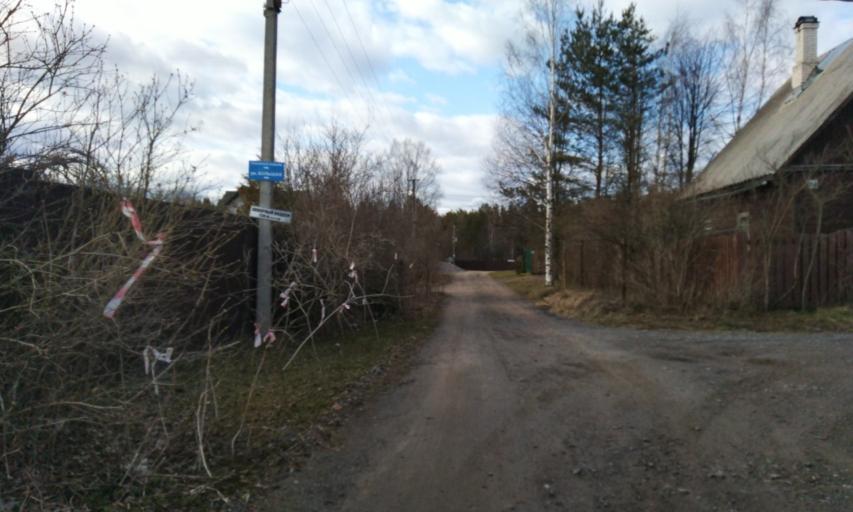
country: RU
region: Leningrad
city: Toksovo
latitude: 60.1299
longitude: 30.4889
